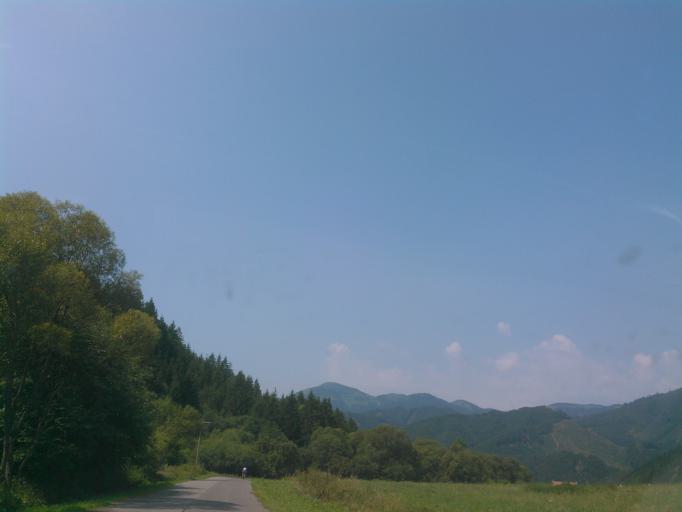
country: SK
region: Zilinsky
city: Ruzomberok
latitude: 48.9462
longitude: 19.2829
